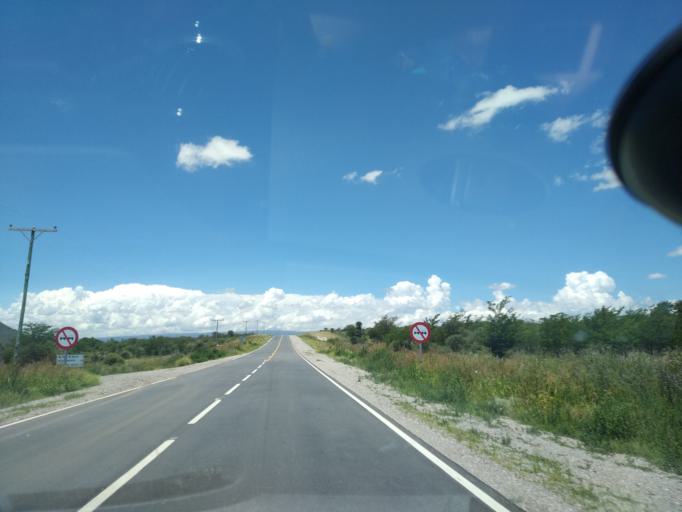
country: AR
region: Cordoba
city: Salsacate
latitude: -31.3599
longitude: -65.1788
